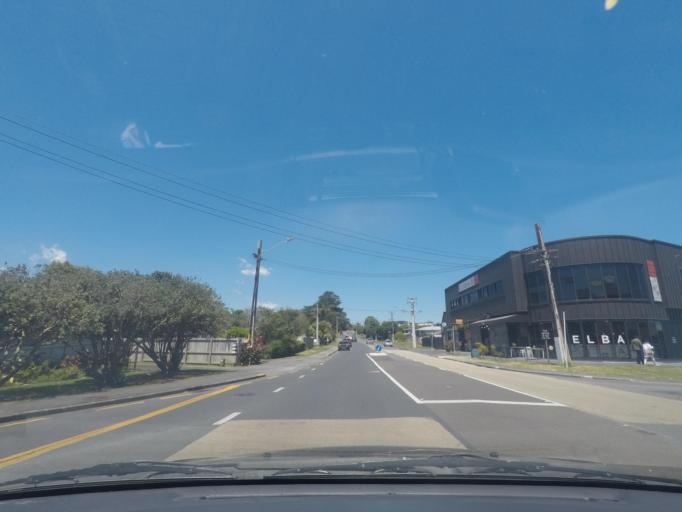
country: NZ
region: Auckland
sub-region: Auckland
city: Waitakere
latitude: -36.9224
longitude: 174.7199
